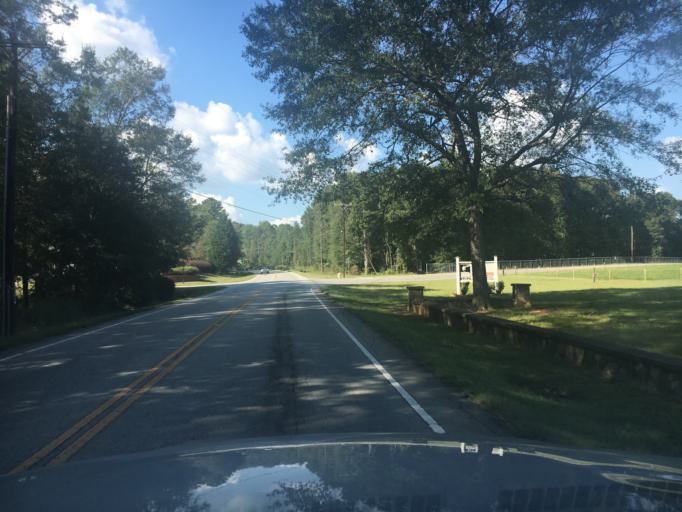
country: US
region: South Carolina
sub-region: Greenville County
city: Fountain Inn
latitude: 34.6539
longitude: -82.2575
